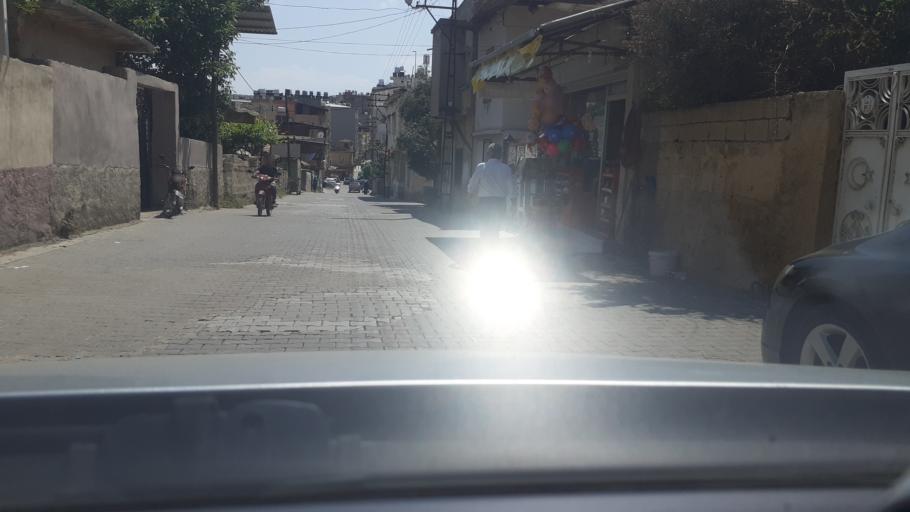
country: TR
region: Hatay
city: Kirikhan
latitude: 36.5016
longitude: 36.3591
